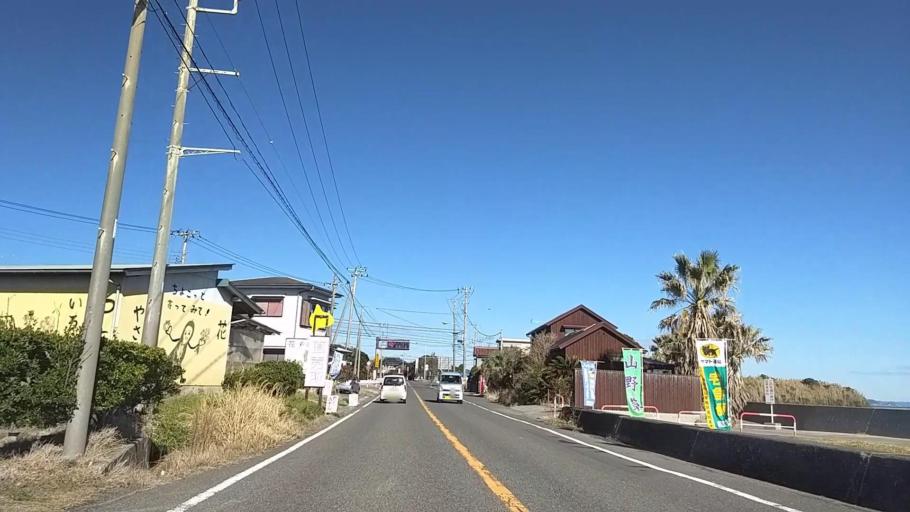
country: JP
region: Chiba
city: Tateyama
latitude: 34.9814
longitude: 139.9668
